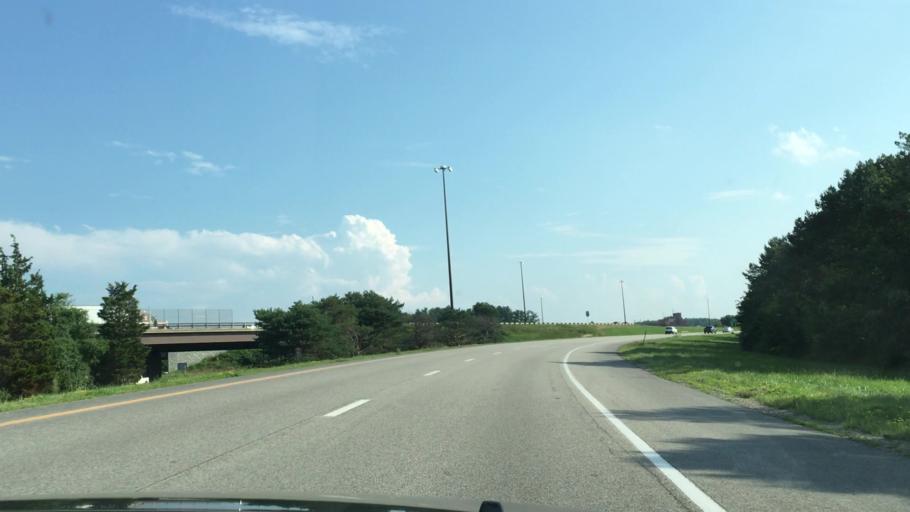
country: US
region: New Hampshire
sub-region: Rockingham County
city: Portsmouth
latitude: 43.0720
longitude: -70.7880
